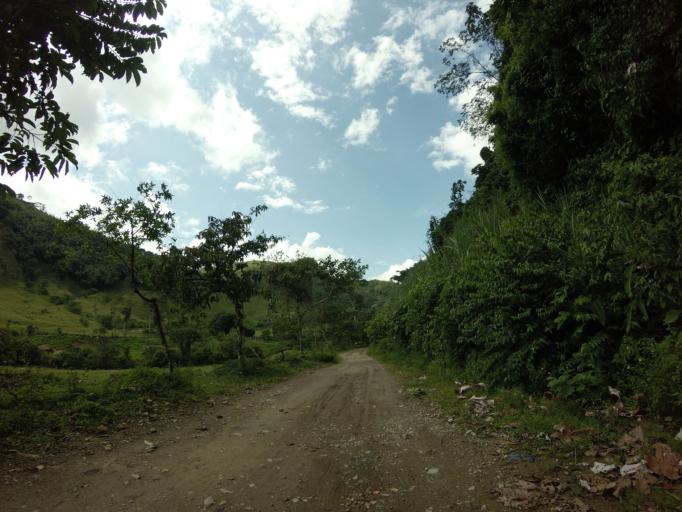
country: CO
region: Antioquia
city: Narino
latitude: 5.5196
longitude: -75.1907
